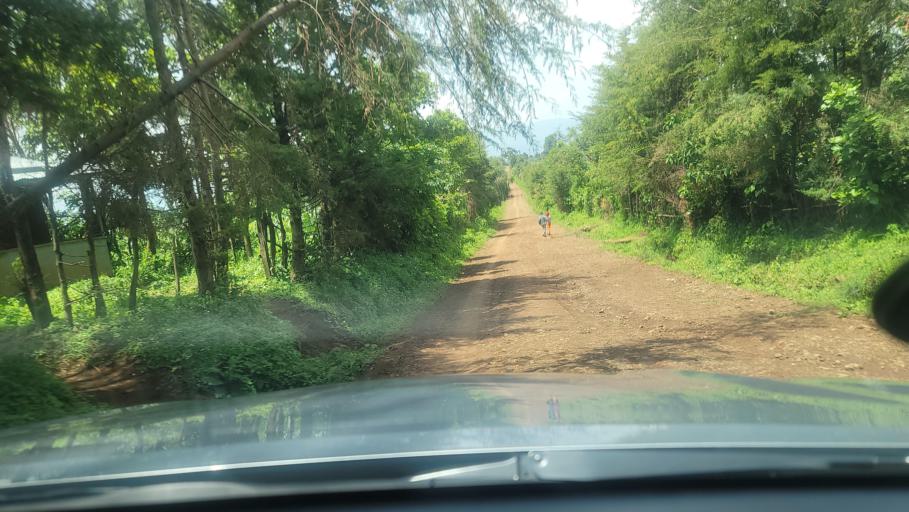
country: ET
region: Oromiya
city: Agaro
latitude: 7.8270
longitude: 36.4076
